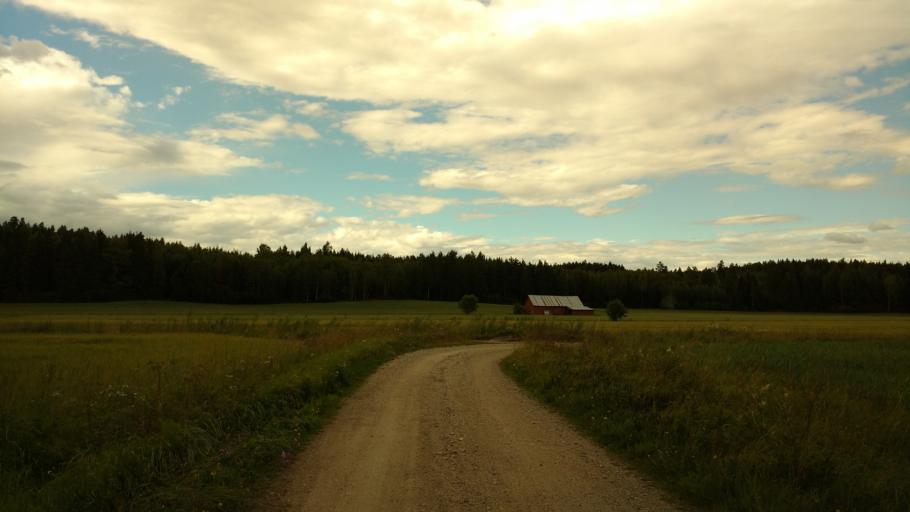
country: FI
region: Varsinais-Suomi
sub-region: Salo
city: Halikko
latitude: 60.4020
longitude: 22.9834
